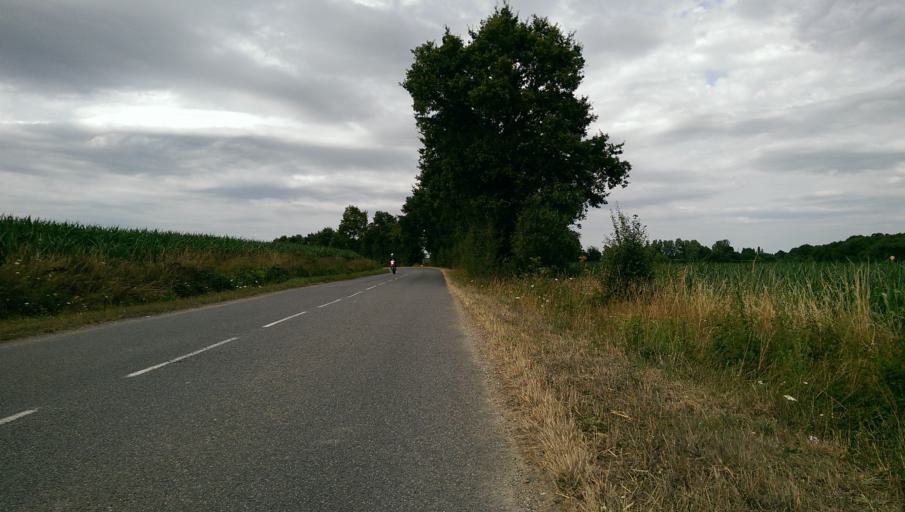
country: FR
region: Pays de la Loire
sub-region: Departement de la Loire-Atlantique
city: Vieillevigne
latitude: 46.9769
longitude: -1.4310
